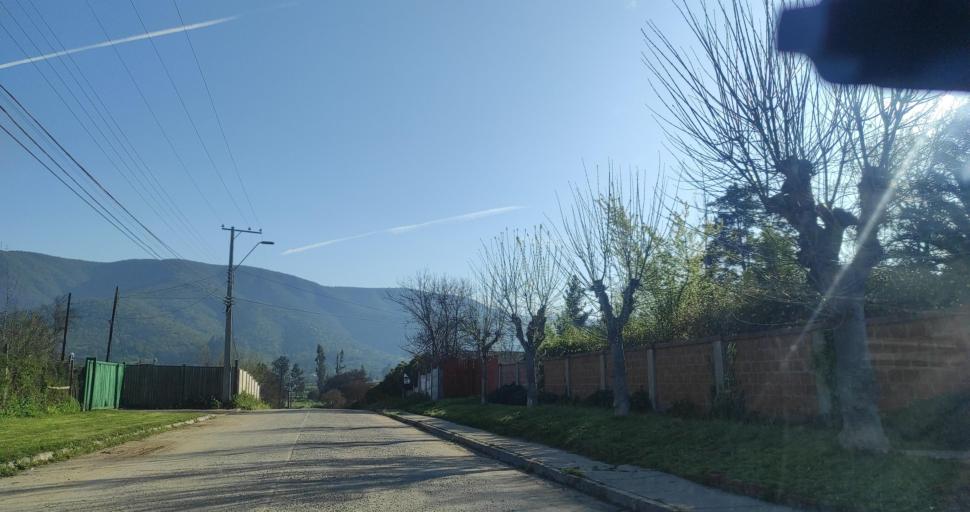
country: CL
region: Valparaiso
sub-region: Provincia de Marga Marga
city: Limache
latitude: -33.0027
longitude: -71.2537
